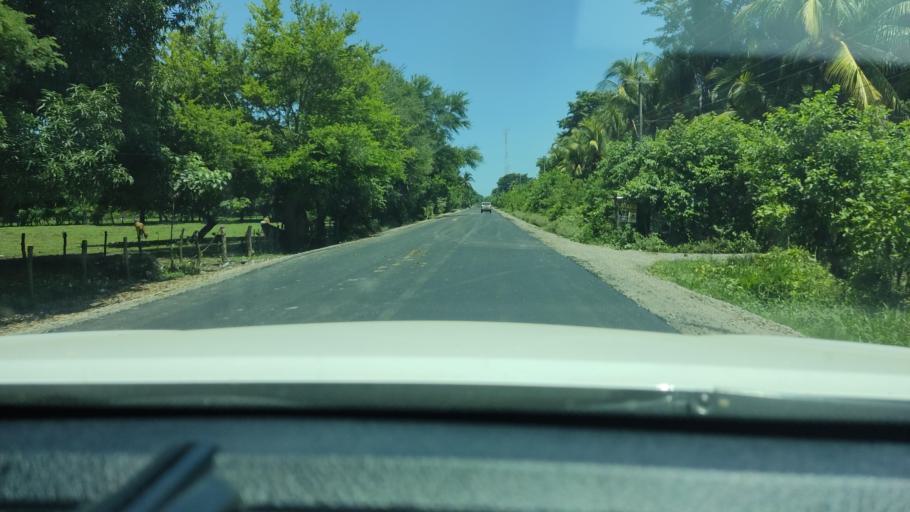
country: SV
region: Ahuachapan
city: San Francisco Menendez
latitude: 13.8325
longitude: -90.1193
